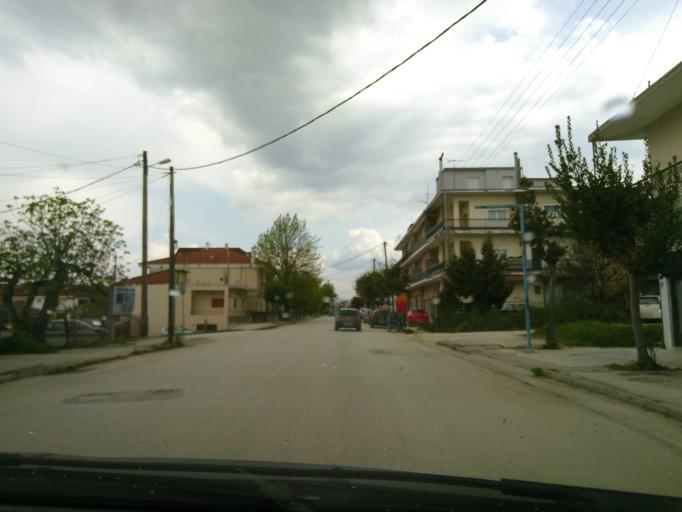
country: GR
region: Epirus
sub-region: Nomos Ioanninon
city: Anatoli
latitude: 39.6452
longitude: 20.8637
